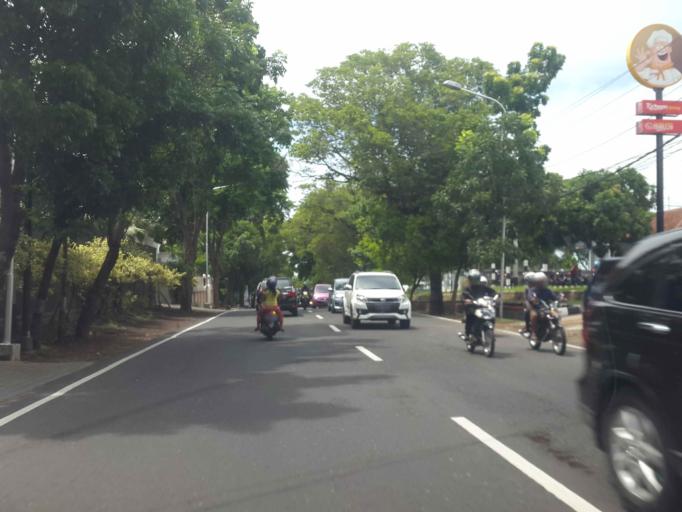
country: ID
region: Central Java
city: Semarang
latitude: -7.0051
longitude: 110.4116
